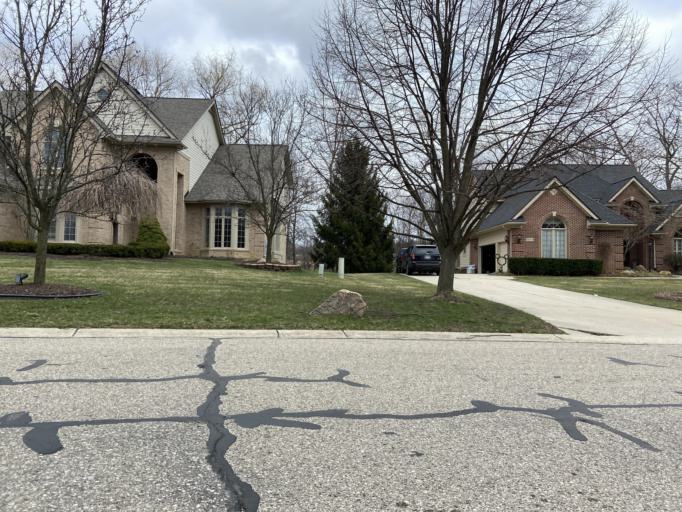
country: US
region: Michigan
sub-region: Oakland County
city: Franklin
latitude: 42.5042
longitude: -83.3231
